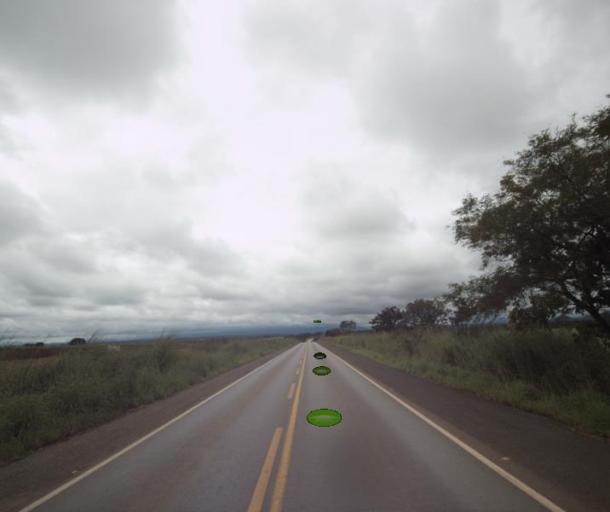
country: BR
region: Goias
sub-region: Uruacu
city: Uruacu
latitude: -14.7140
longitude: -49.0896
